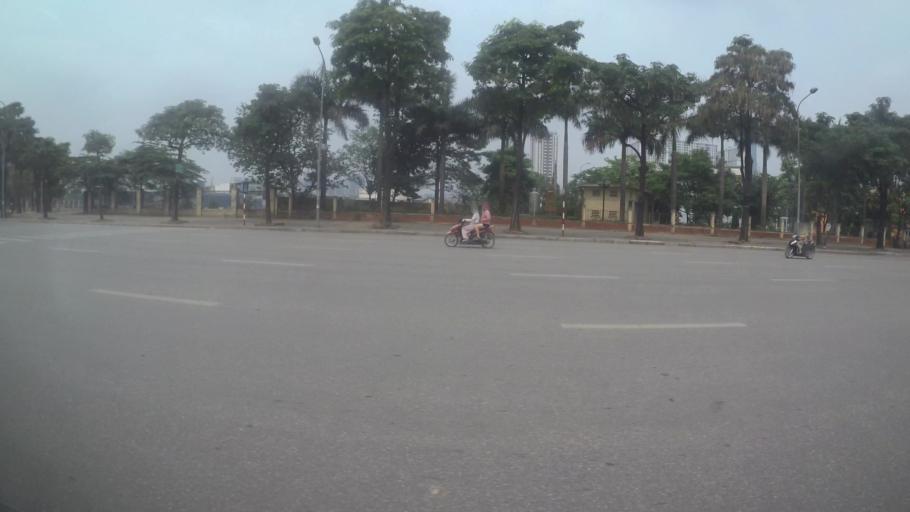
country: VN
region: Ha Noi
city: Cau Dien
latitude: 21.0168
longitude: 105.7678
